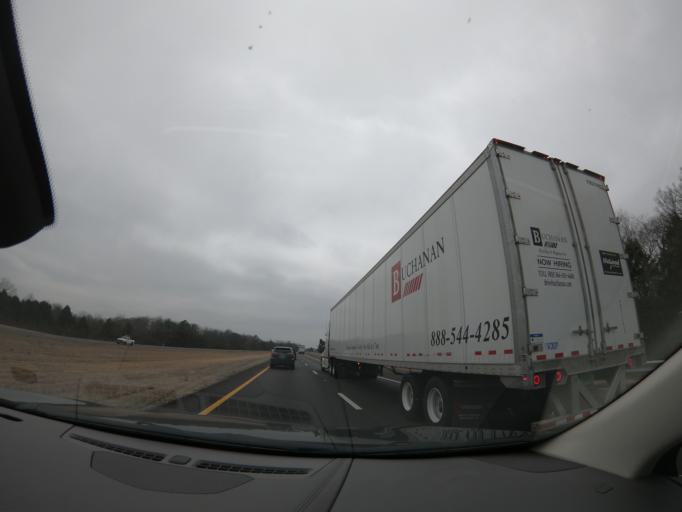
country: US
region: Tennessee
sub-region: Rutherford County
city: Plainview
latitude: 35.7724
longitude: -86.3633
